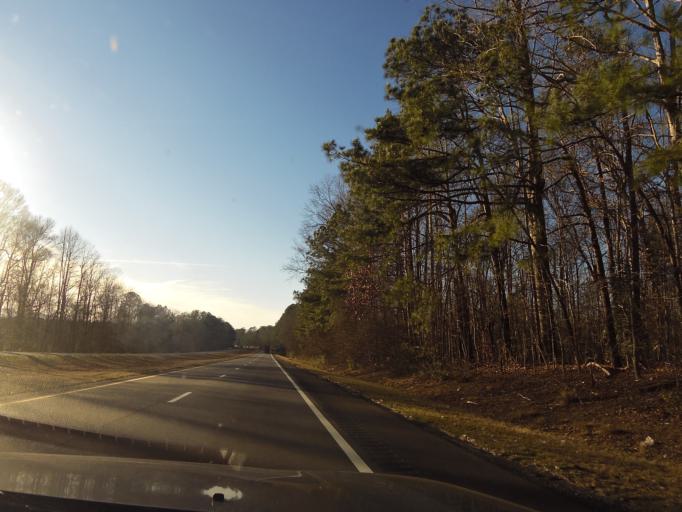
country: US
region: Virginia
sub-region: City of Franklin
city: Franklin
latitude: 36.6502
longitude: -76.8581
